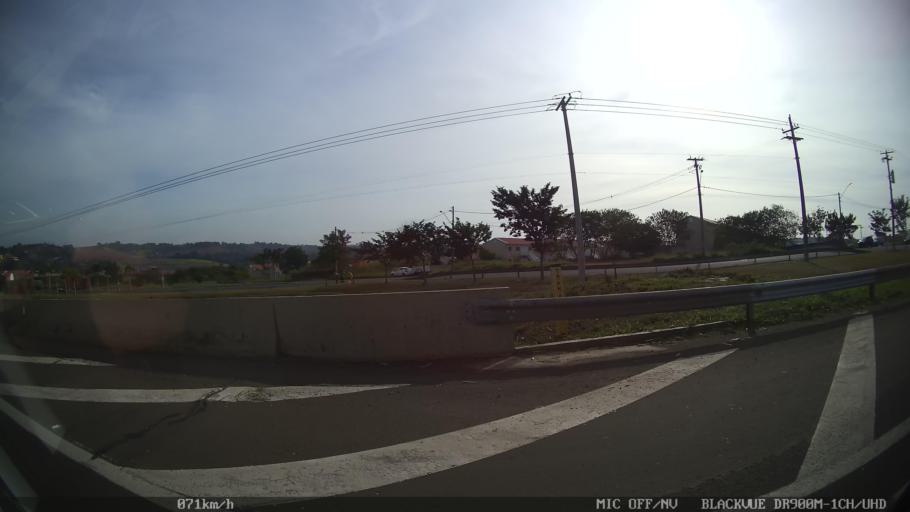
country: BR
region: Sao Paulo
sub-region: Piracicaba
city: Piracicaba
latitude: -22.6785
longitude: -47.7136
